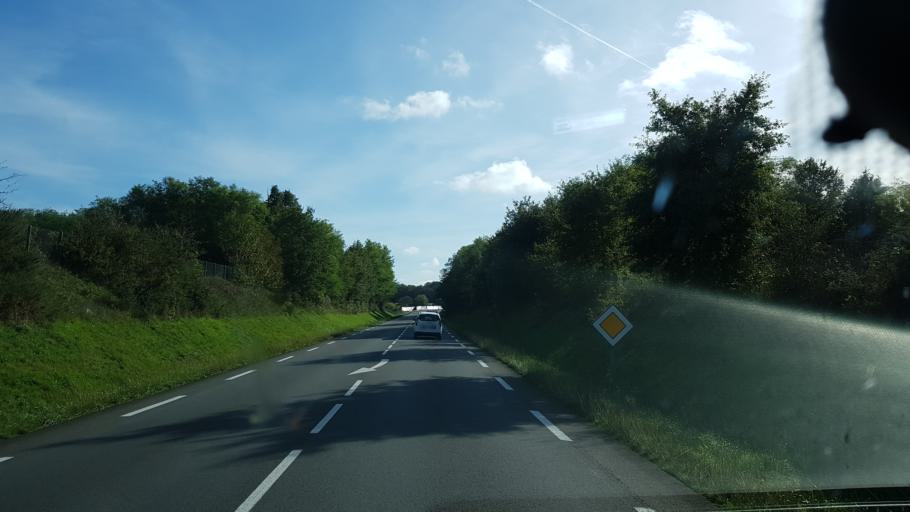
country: FR
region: Poitou-Charentes
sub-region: Departement de la Charente
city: Saint-Claud
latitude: 45.8653
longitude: 0.4659
